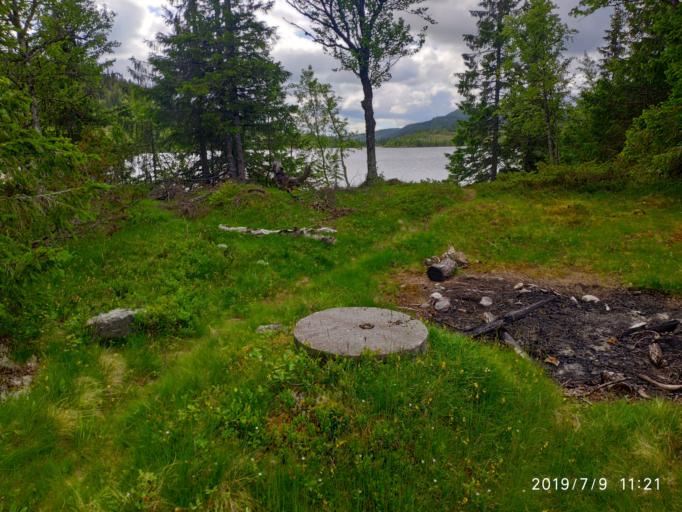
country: NO
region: Buskerud
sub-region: Nore og Uvdal
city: Rodberg
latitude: 60.3336
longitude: 9.1795
